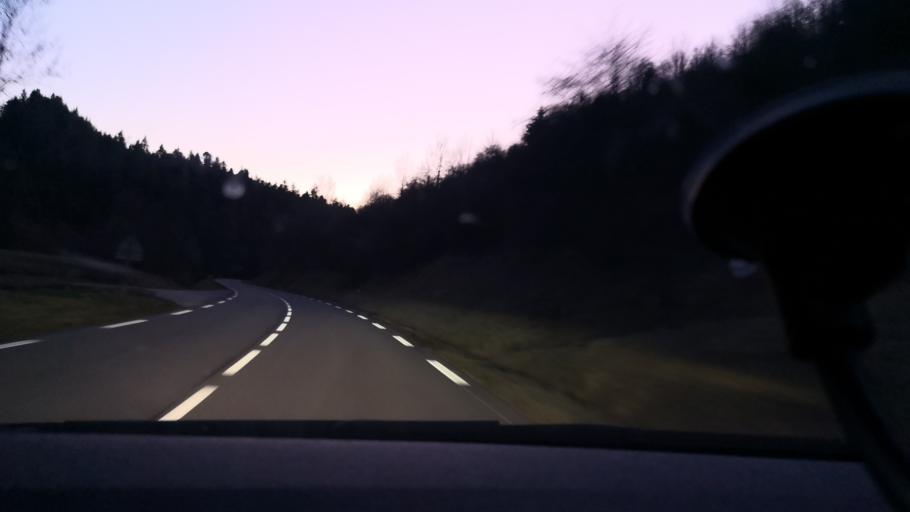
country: FR
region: Franche-Comte
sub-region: Departement du Jura
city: Champagnole
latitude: 46.7712
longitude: 5.9854
